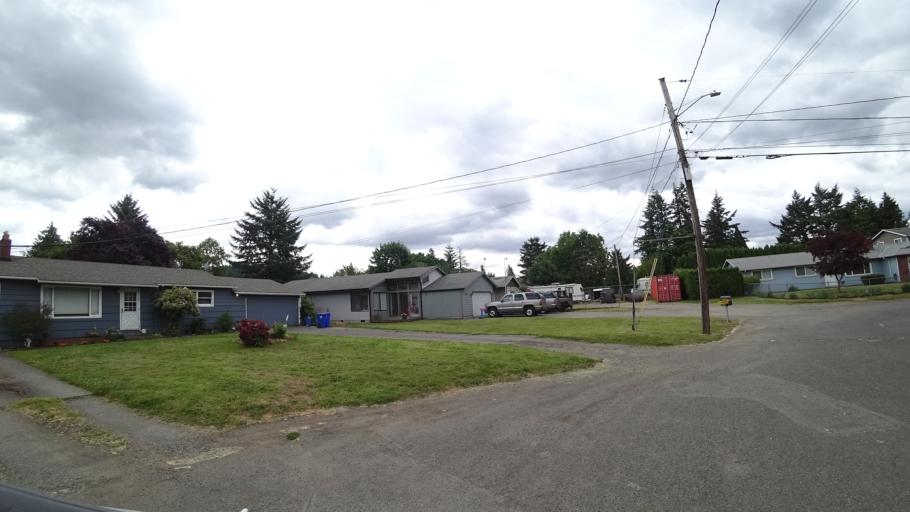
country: US
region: Oregon
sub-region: Multnomah County
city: Lents
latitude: 45.4950
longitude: -122.5287
